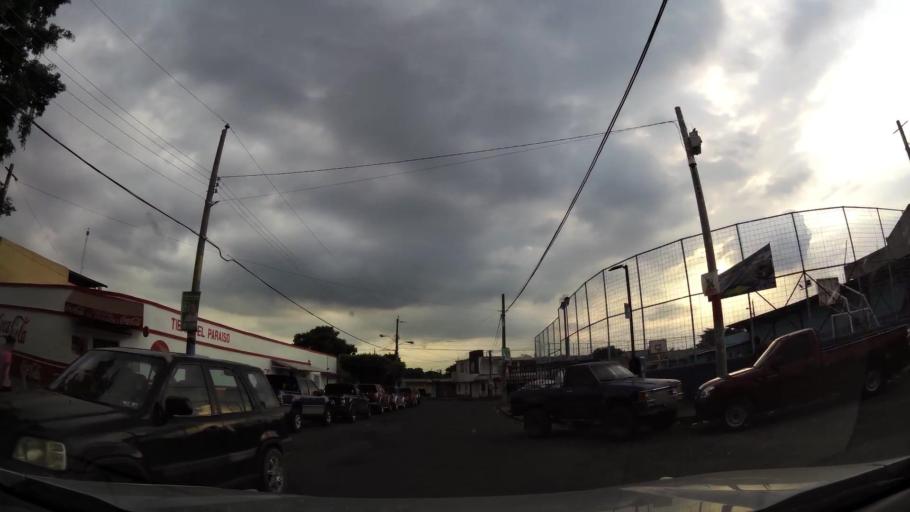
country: GT
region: Escuintla
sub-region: Municipio de Escuintla
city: Escuintla
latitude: 14.2898
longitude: -90.7809
